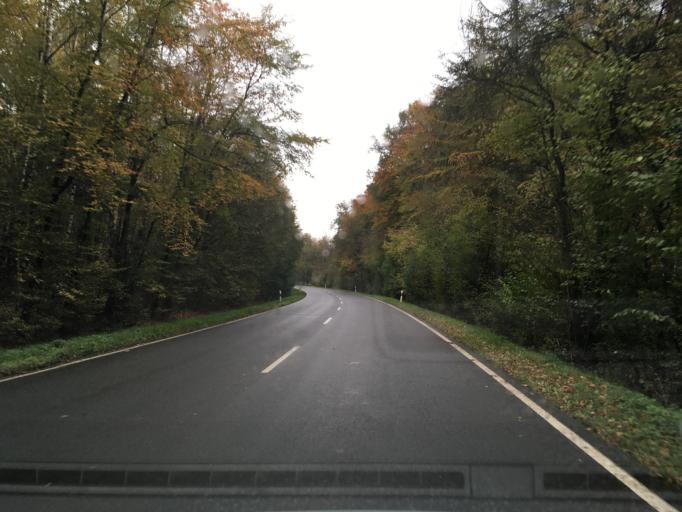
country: DE
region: North Rhine-Westphalia
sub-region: Regierungsbezirk Munster
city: Velen
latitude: 51.8770
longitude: 7.0029
